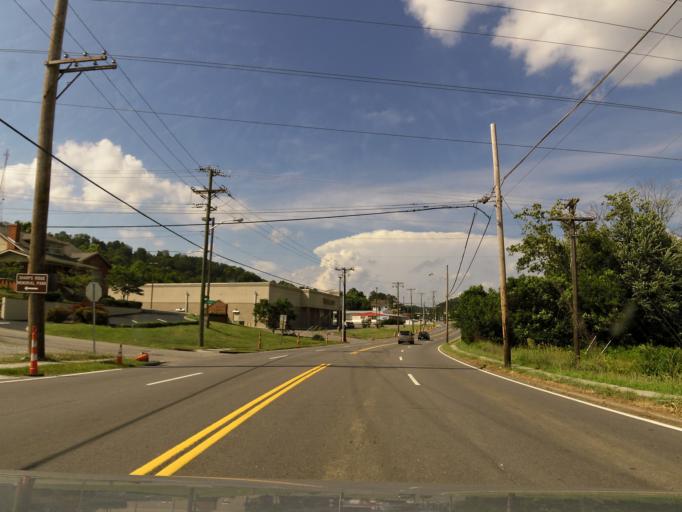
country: US
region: Tennessee
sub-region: Knox County
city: Knoxville
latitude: 36.0074
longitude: -83.9266
